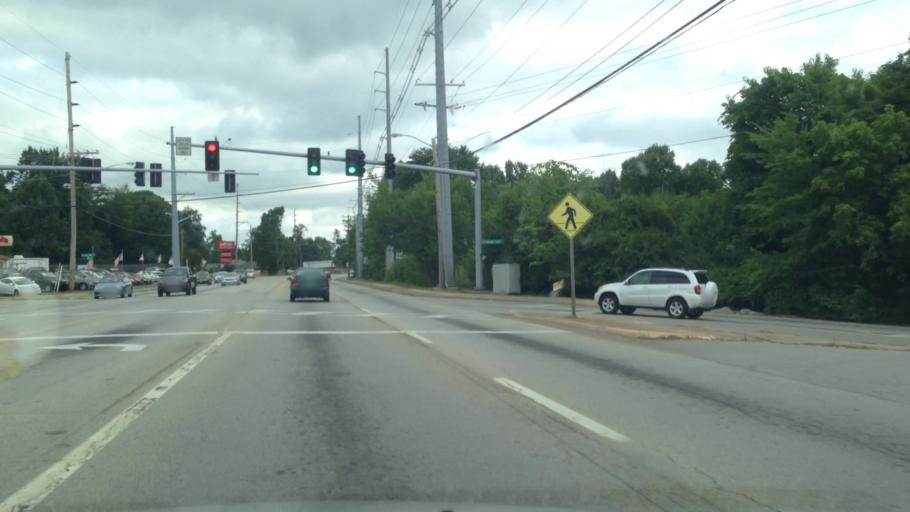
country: US
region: Virginia
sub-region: City of Danville
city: Danville
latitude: 36.6174
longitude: -79.4058
